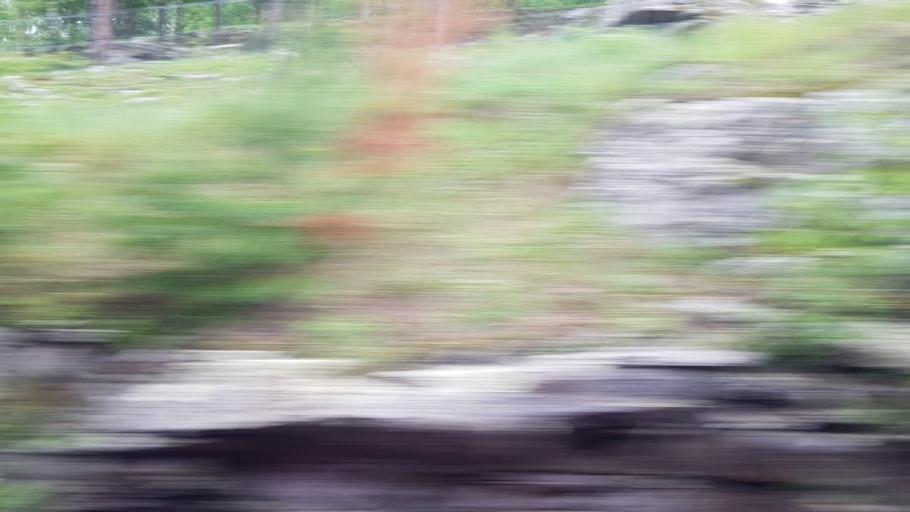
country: NO
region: Oppland
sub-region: Sor-Fron
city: Hundorp
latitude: 61.5548
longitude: 9.9450
